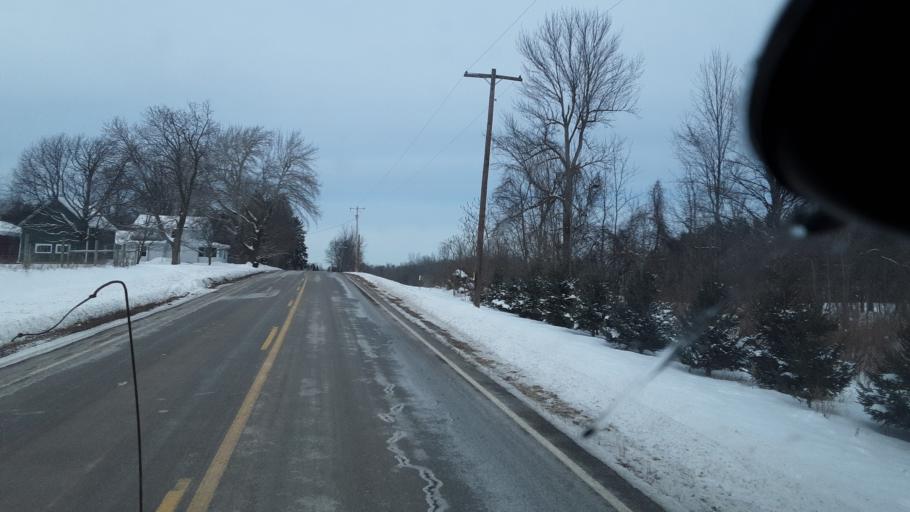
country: US
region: New York
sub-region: Wayne County
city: Lyons
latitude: 43.0954
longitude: -77.0423
